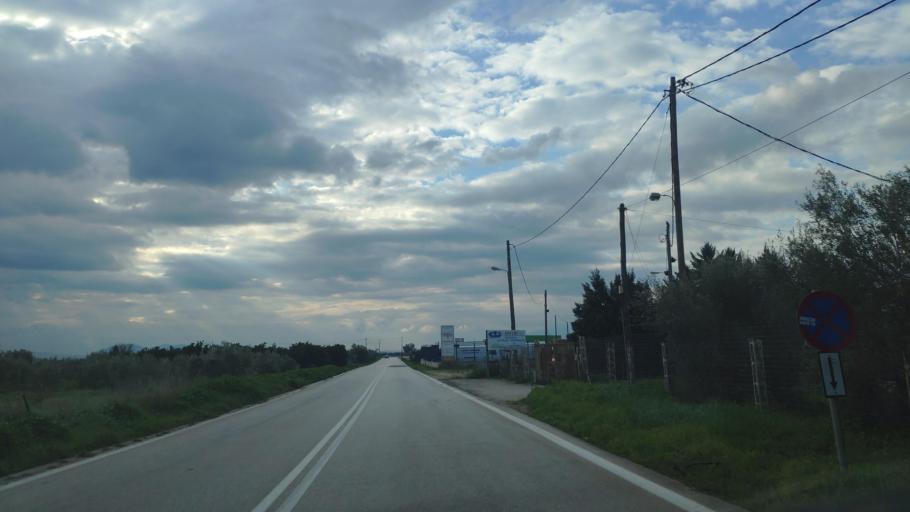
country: GR
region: Peloponnese
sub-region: Nomos Argolidos
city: Koutsopodi
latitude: 37.7145
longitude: 22.7252
